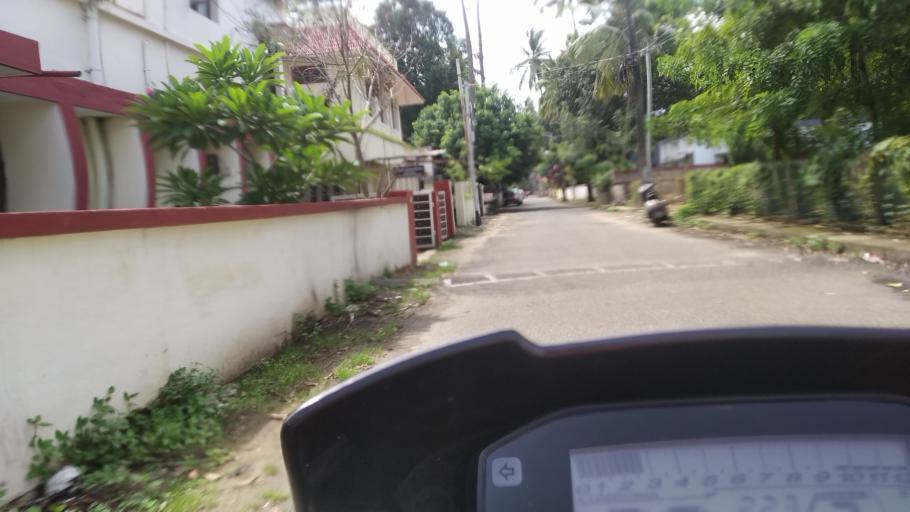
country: IN
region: Kerala
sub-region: Ernakulam
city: Cochin
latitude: 9.9615
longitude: 76.2985
